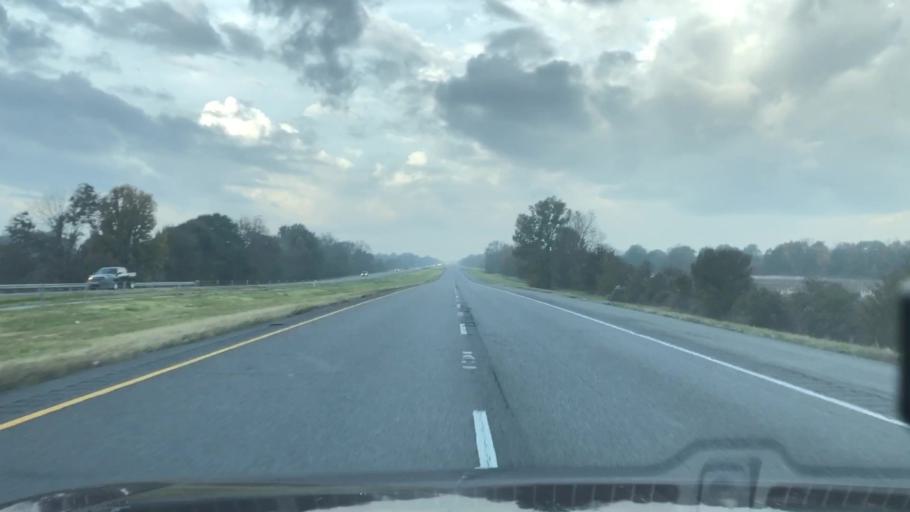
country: US
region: Louisiana
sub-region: Madison Parish
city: Tallulah
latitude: 32.4054
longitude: -91.2280
